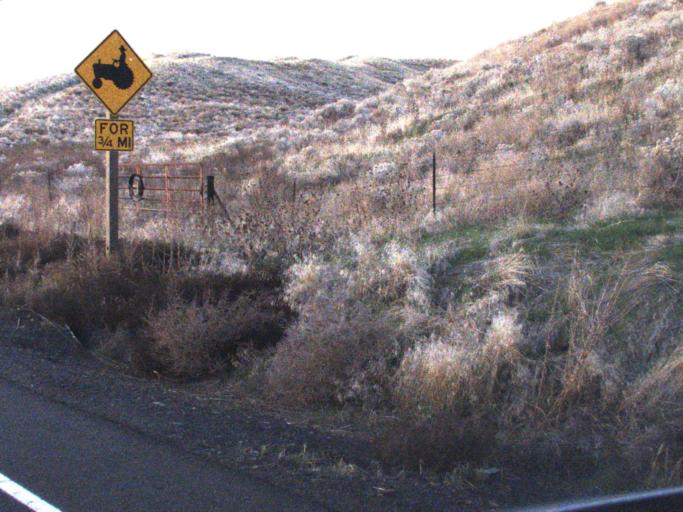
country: US
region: Washington
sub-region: Garfield County
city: Pomeroy
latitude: 46.6442
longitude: -117.8095
